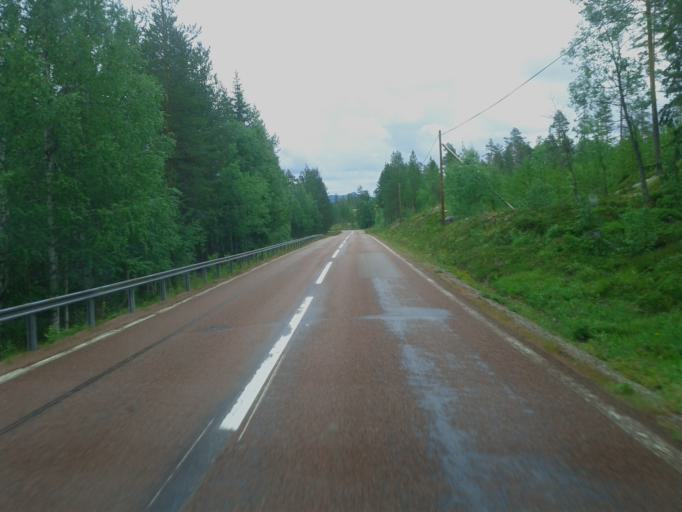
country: NO
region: Hedmark
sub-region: Trysil
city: Innbygda
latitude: 61.8526
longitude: 12.6362
